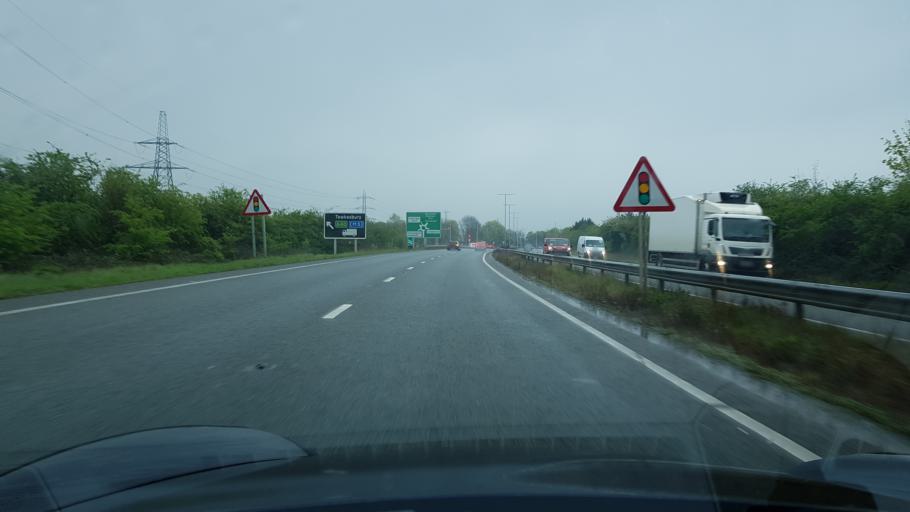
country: GB
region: England
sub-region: Gloucestershire
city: Barnwood
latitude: 51.8814
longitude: -2.2032
